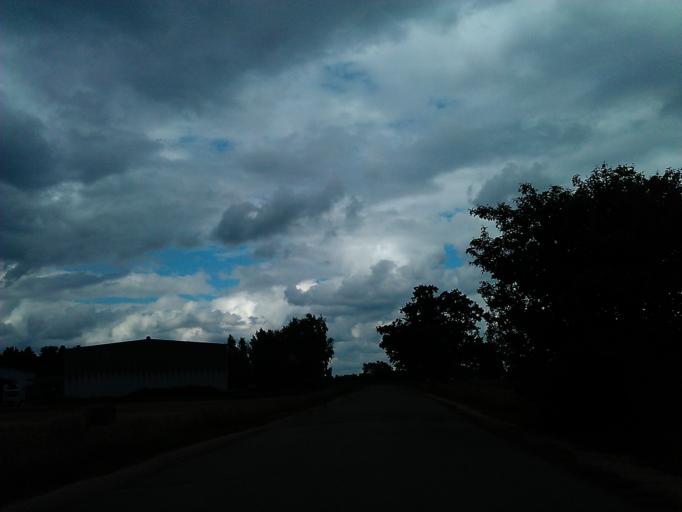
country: LV
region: Adazi
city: Adazi
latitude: 57.0841
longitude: 24.2958
